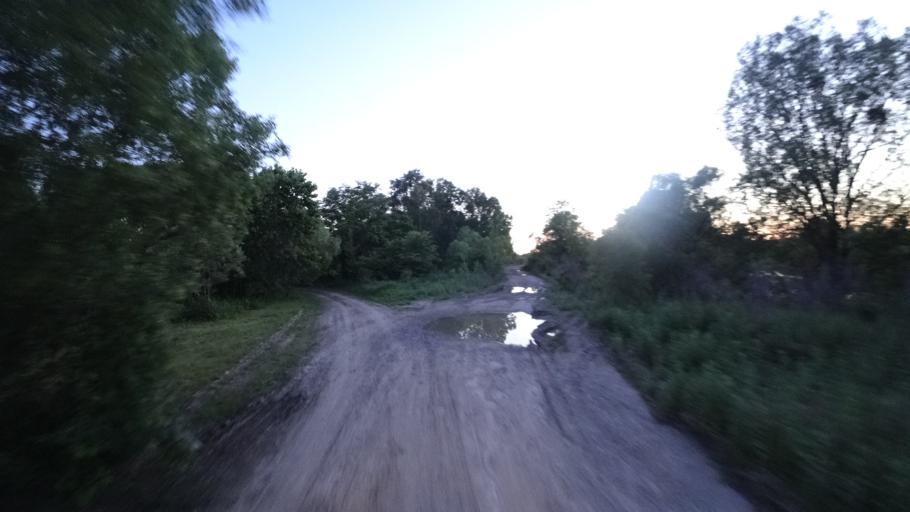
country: RU
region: Khabarovsk Krai
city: Khor
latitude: 47.8575
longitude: 134.9373
